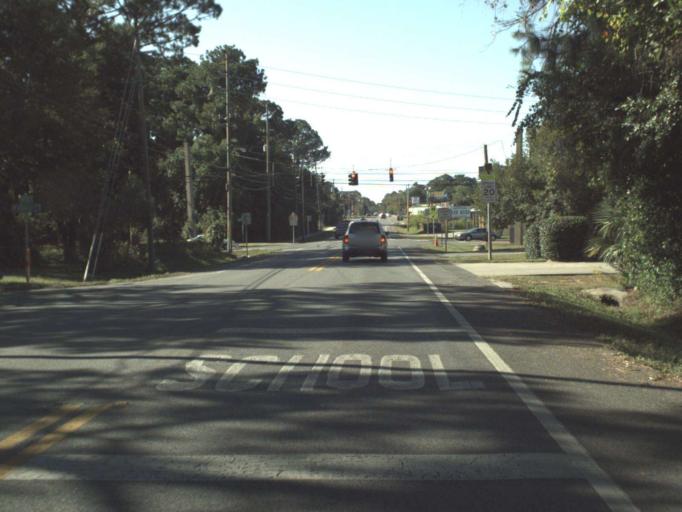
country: US
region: Florida
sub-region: Bay County
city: Pretty Bayou
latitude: 30.1878
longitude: -85.6750
